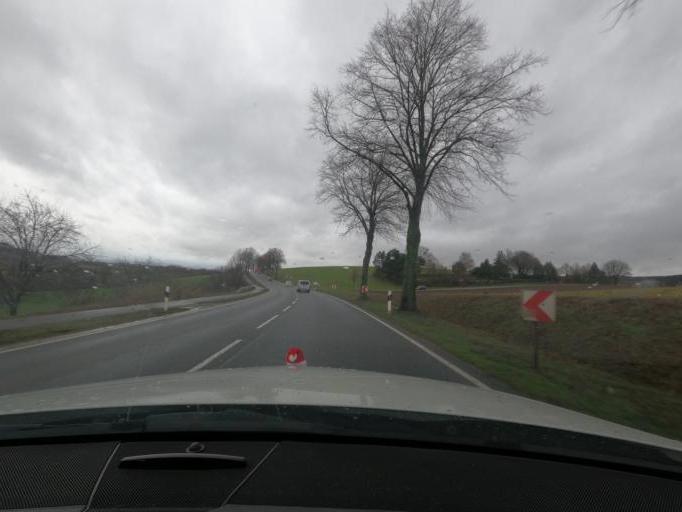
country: DE
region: Lower Saxony
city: Kreiensen
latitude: 51.7755
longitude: 9.9423
